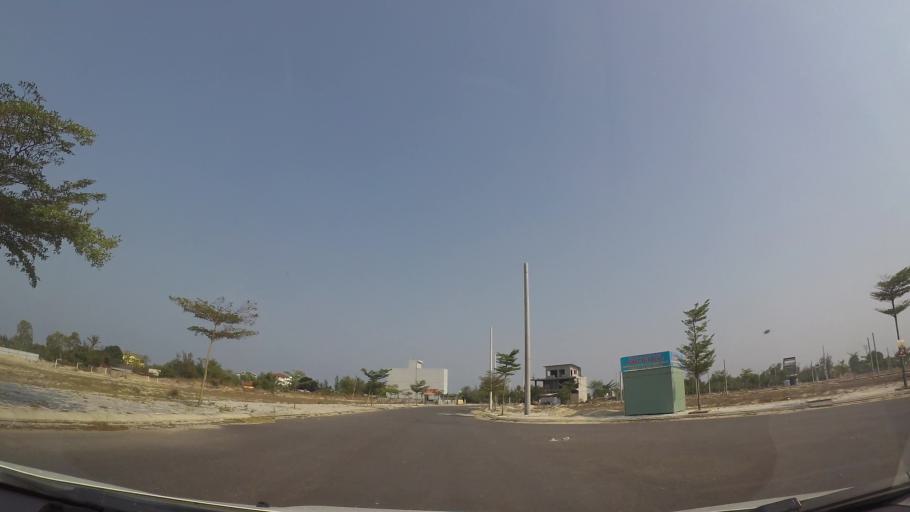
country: VN
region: Da Nang
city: Ngu Hanh Son
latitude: 15.9564
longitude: 108.2759
